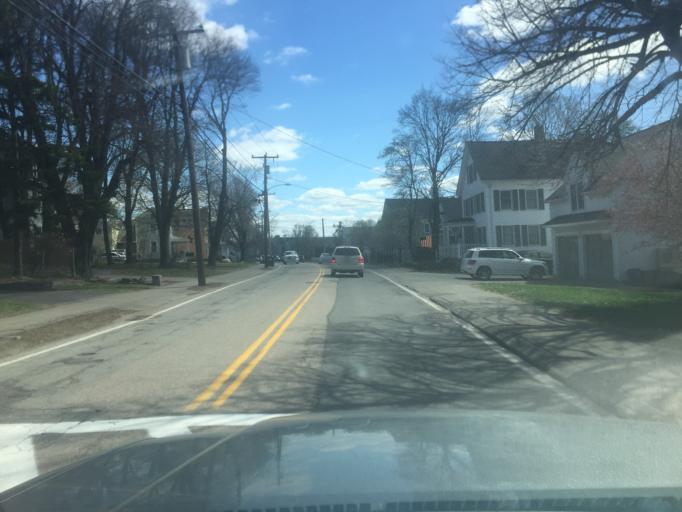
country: US
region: Massachusetts
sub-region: Norfolk County
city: Medfield
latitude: 42.1911
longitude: -71.3092
